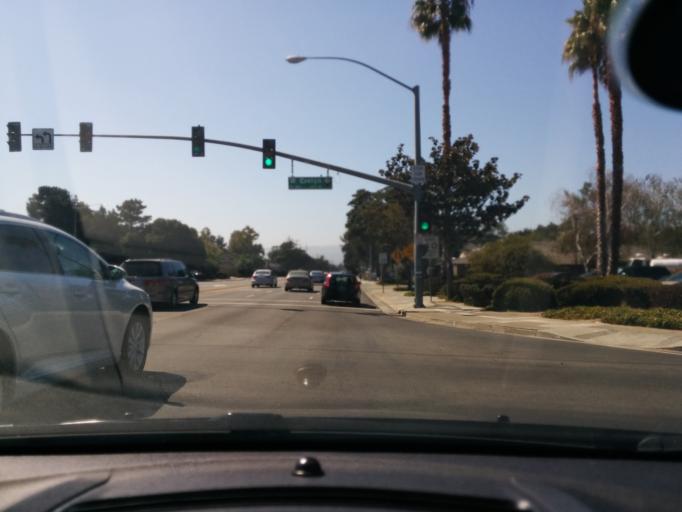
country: US
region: California
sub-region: Santa Clara County
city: Sunnyvale
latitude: 37.3832
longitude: -122.0448
